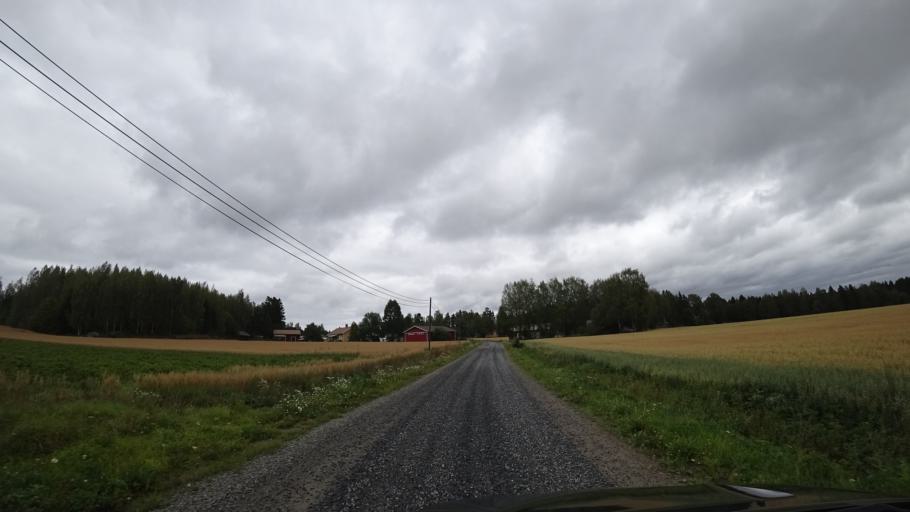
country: FI
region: Haeme
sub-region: Haemeenlinna
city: Lammi
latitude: 61.1293
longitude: 24.9864
